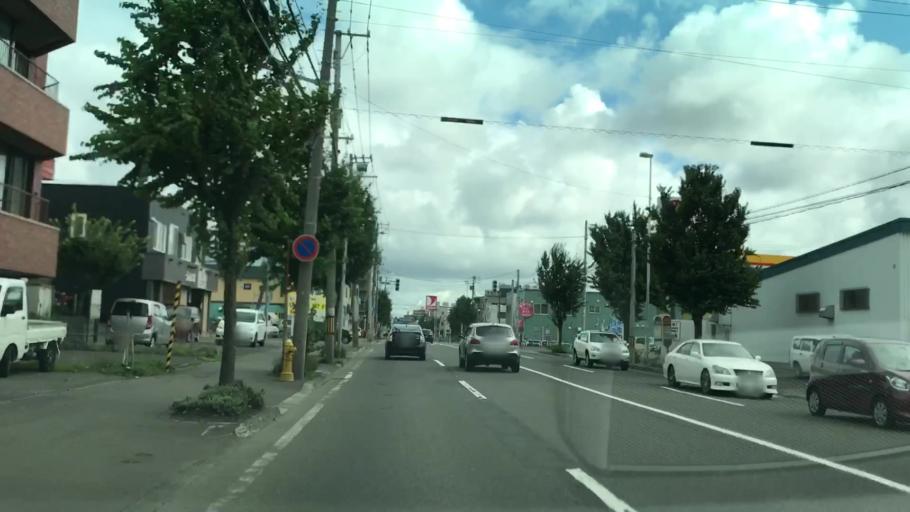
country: JP
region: Hokkaido
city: Sapporo
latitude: 43.0838
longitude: 141.3234
